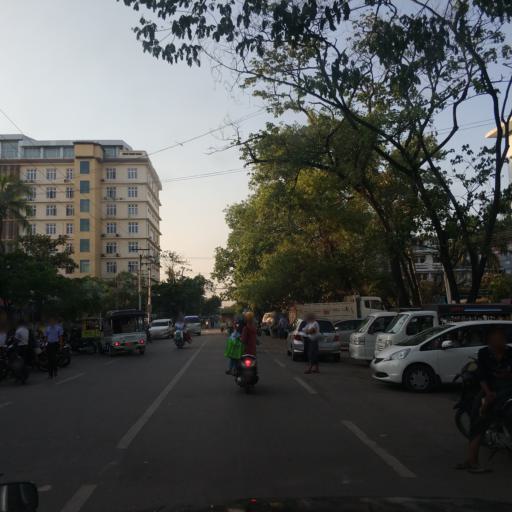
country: MM
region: Mandalay
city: Mandalay
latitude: 21.9759
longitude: 96.0934
